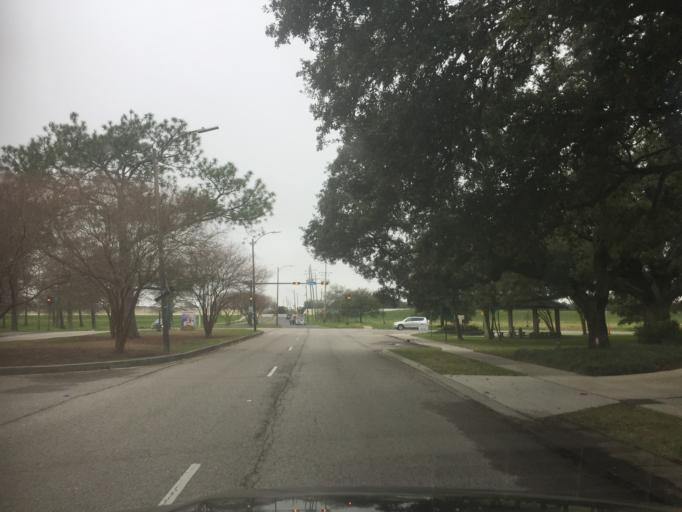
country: US
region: Louisiana
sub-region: Jefferson Parish
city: Metairie
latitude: 30.0188
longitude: -90.0959
